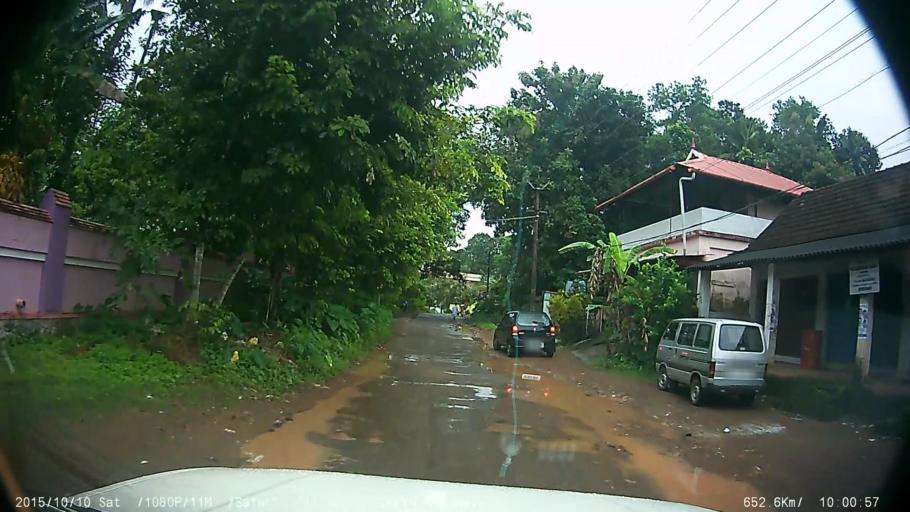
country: IN
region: Kerala
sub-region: Kottayam
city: Kottayam
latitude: 9.6393
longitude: 76.5365
